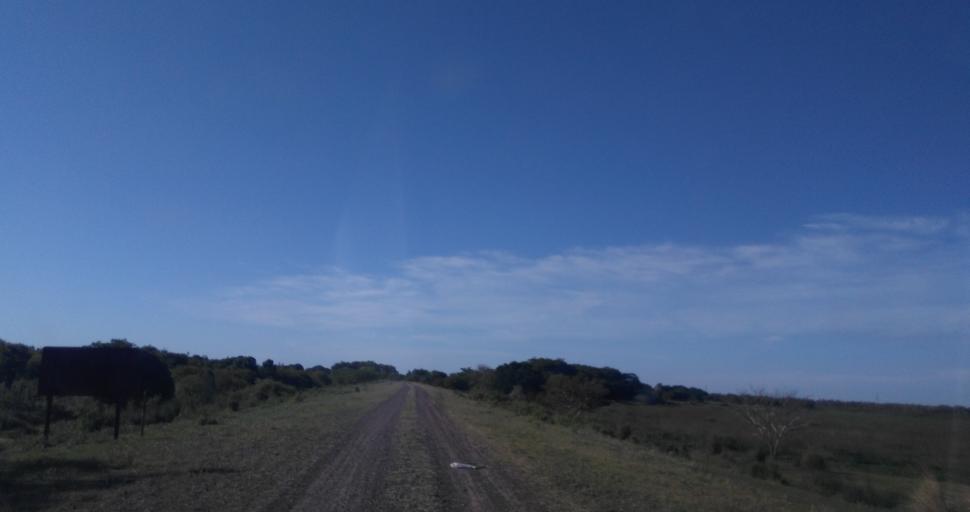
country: AR
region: Chaco
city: Barranqueras
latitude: -27.4314
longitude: -58.9248
